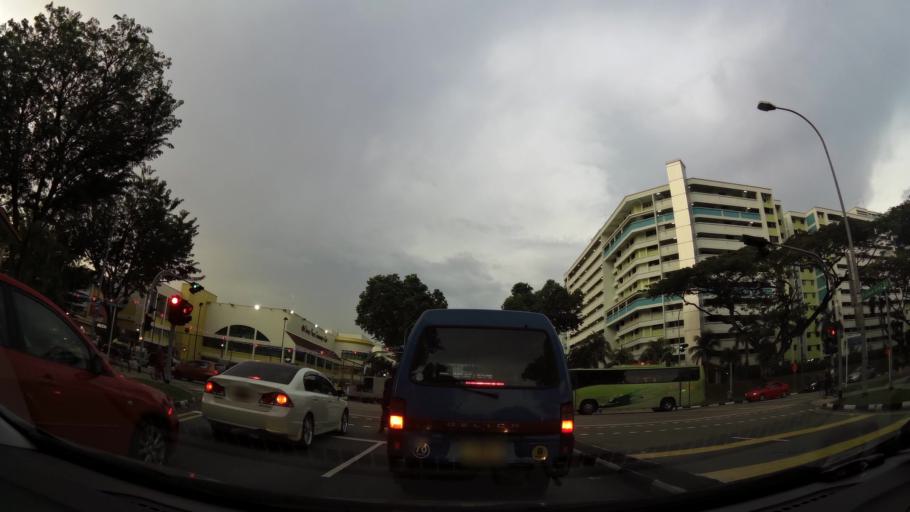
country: MY
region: Johor
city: Kampung Pasir Gudang Baru
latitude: 1.4301
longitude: 103.8297
